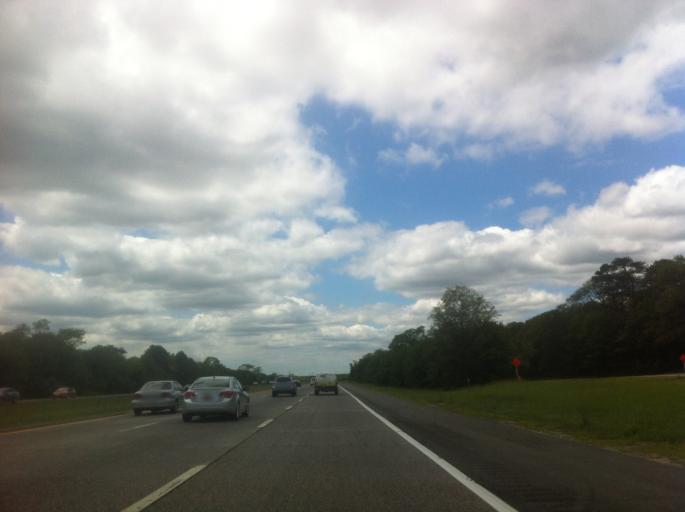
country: US
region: New York
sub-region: Suffolk County
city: Yaphank
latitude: 40.8428
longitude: -72.8933
